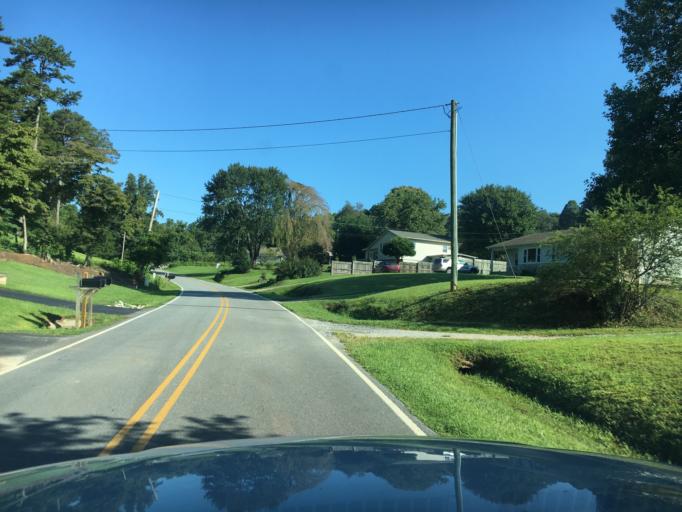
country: US
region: North Carolina
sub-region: McDowell County
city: West Marion
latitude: 35.6487
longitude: -82.0214
